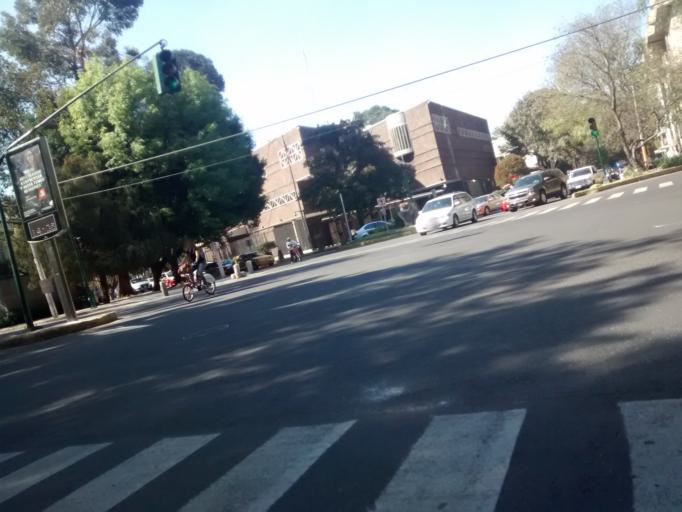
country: MX
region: Mexico City
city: Miguel Hidalgo
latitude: 19.4284
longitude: -99.1853
